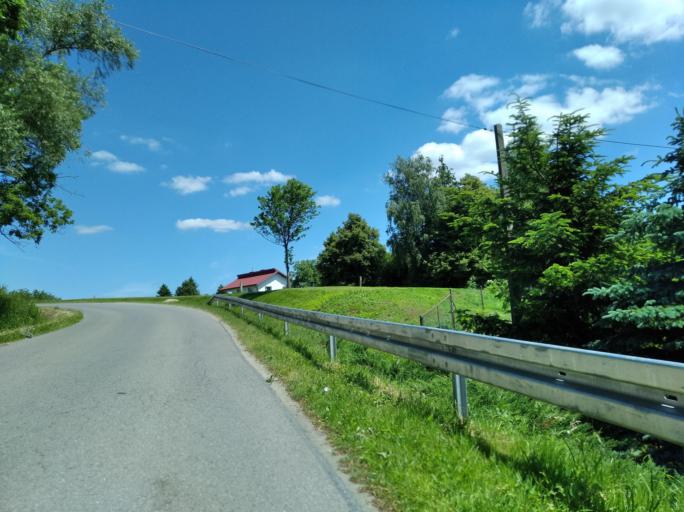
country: PL
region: Subcarpathian Voivodeship
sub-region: Powiat jasielski
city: Osiek Jasielski
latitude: 49.6670
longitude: 21.5438
